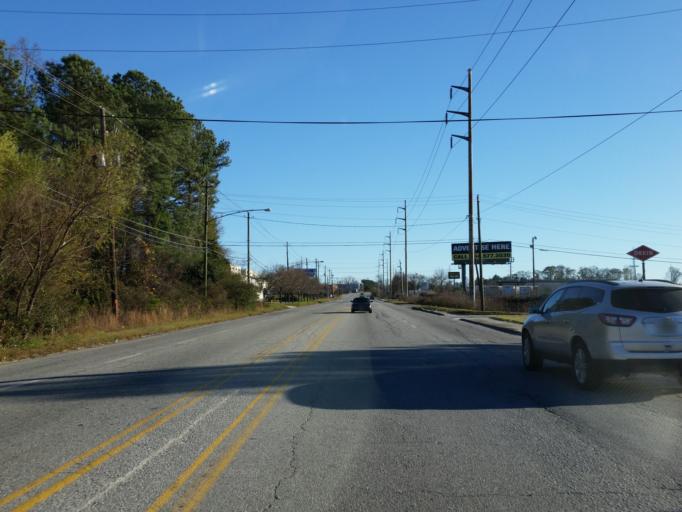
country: US
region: Georgia
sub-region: Fulton County
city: Atlanta
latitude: 33.7940
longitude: -84.4315
